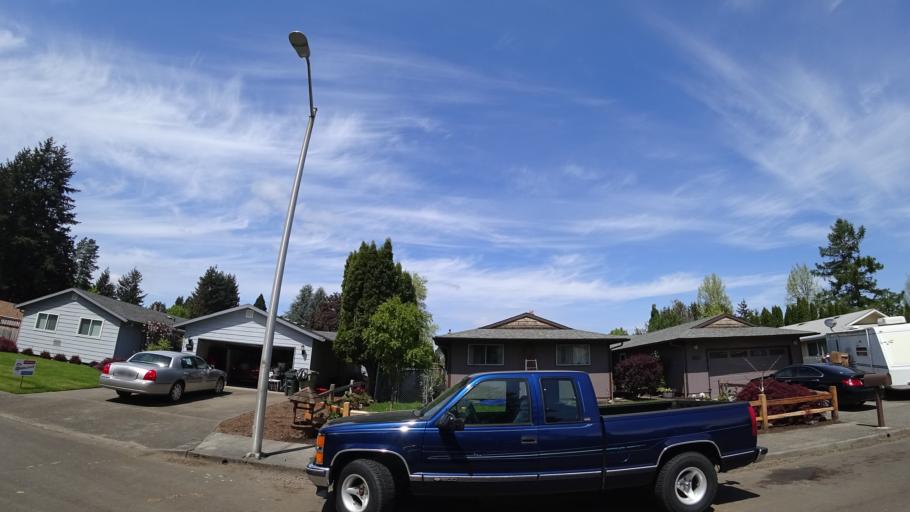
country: US
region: Oregon
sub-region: Washington County
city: Aloha
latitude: 45.4782
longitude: -122.8832
